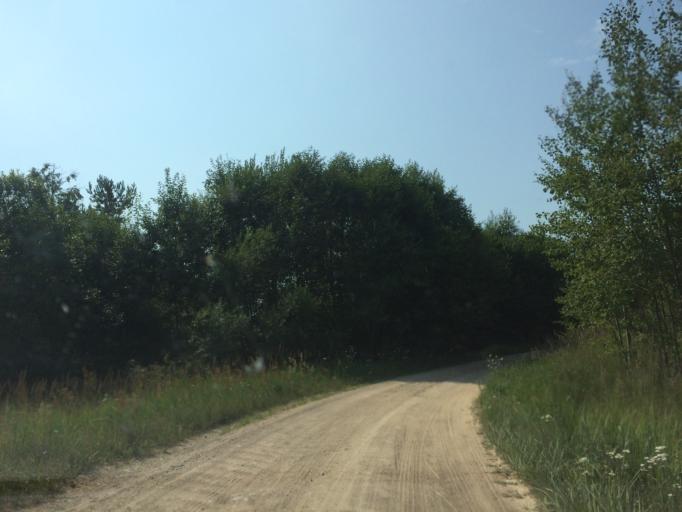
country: LV
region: Ludzas Rajons
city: Ludza
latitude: 56.5382
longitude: 27.5829
